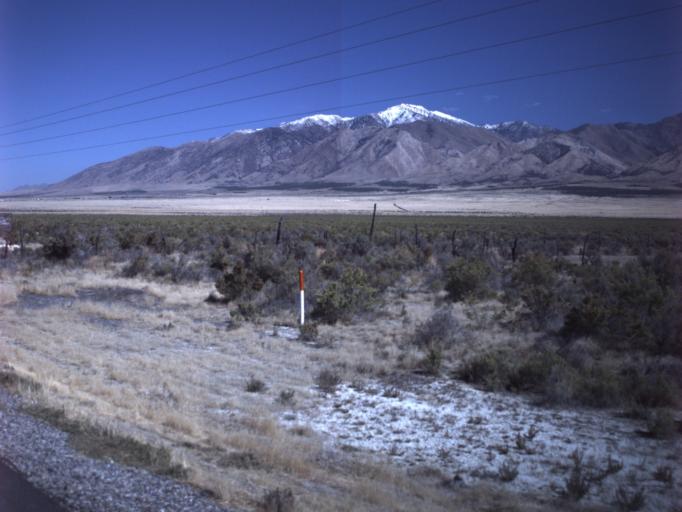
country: US
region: Utah
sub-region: Tooele County
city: Grantsville
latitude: 40.3461
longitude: -112.7451
